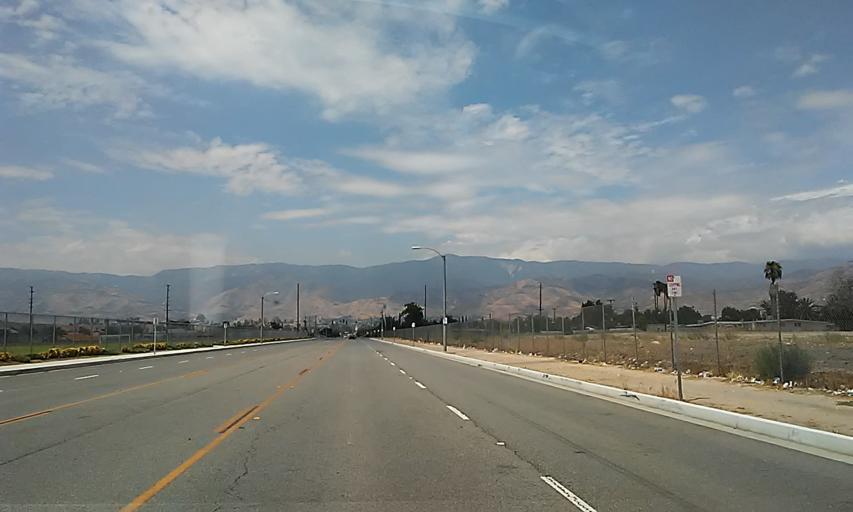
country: US
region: California
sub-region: San Bernardino County
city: San Bernardino
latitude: 34.1131
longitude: -117.2524
